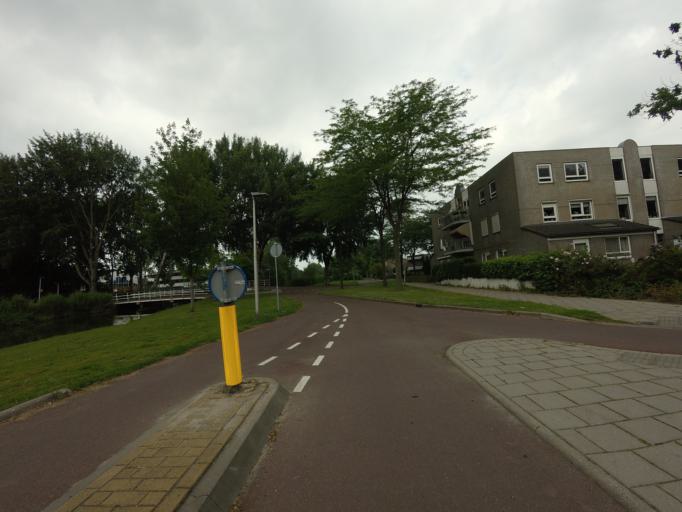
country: NL
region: South Holland
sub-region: Gemeente Krimpen aan den IJssel
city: Krimpen aan den IJssel
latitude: 51.9202
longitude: 4.6052
